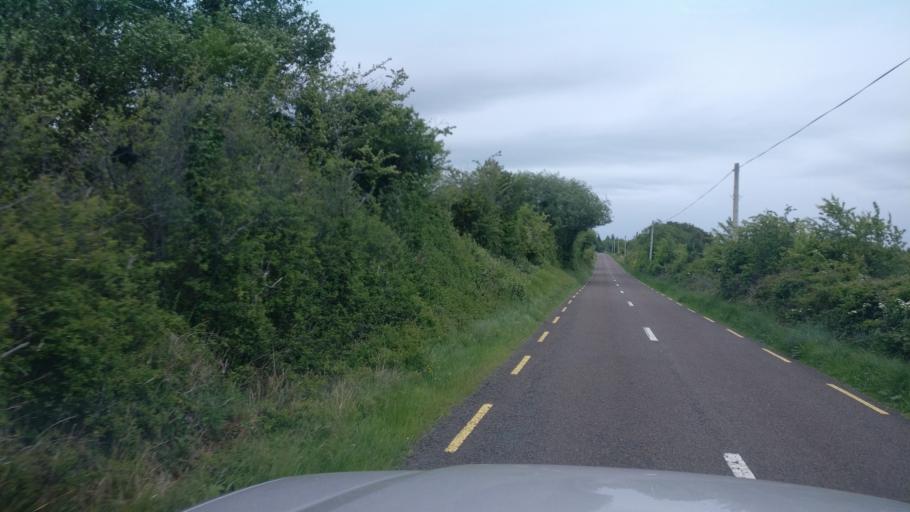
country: IE
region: Connaught
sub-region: County Galway
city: Loughrea
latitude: 53.0848
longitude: -8.5090
